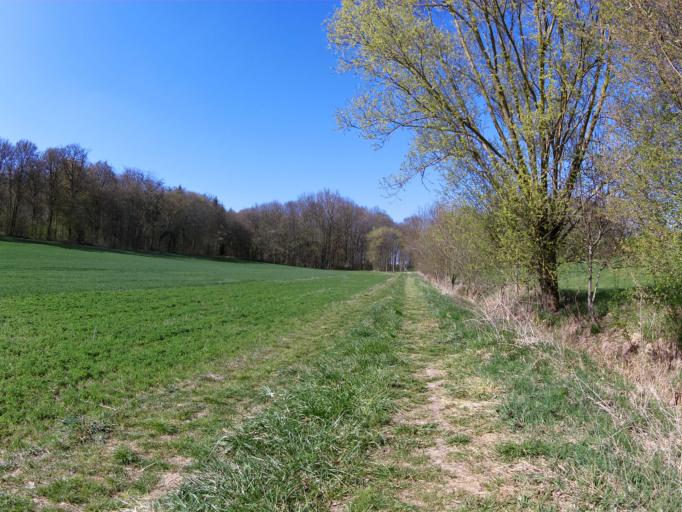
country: DE
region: Bavaria
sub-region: Regierungsbezirk Unterfranken
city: Kurnach
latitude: 49.8255
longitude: 10.0503
